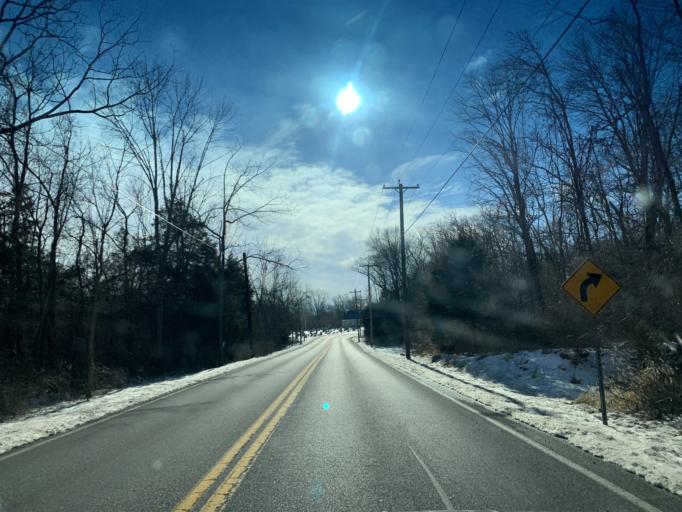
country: US
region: Pennsylvania
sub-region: York County
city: Dover
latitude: 40.0548
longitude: -76.9279
